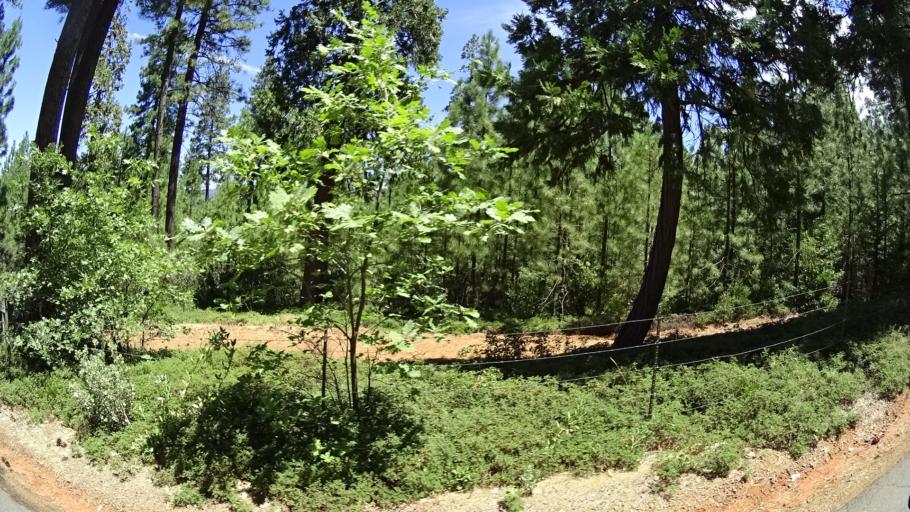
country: US
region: California
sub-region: Calaveras County
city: Forest Meadows
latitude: 38.1978
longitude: -120.4180
